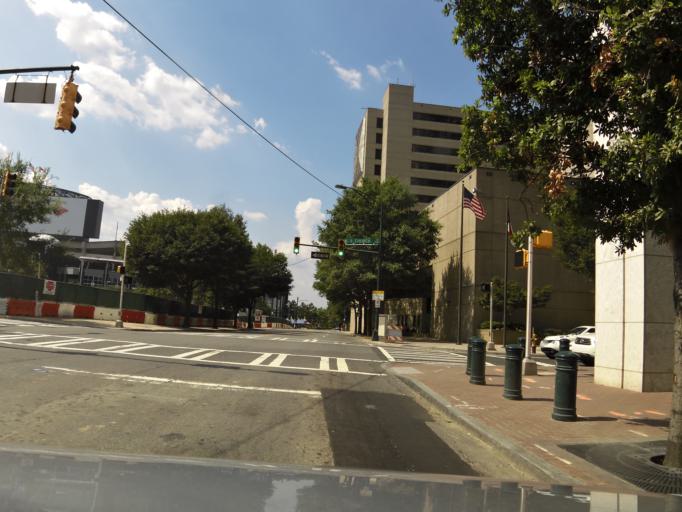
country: US
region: North Carolina
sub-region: Mecklenburg County
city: Charlotte
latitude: 35.2243
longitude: -80.8492
